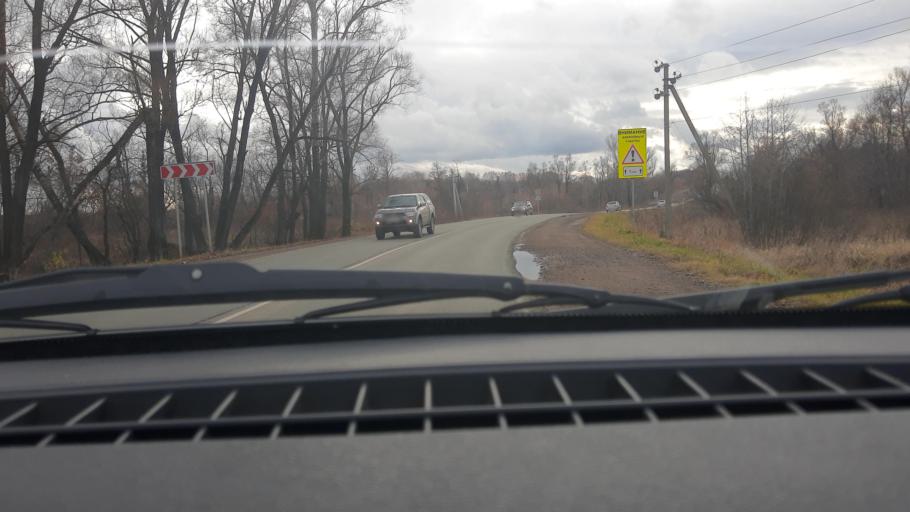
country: RU
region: Bashkortostan
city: Iglino
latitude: 54.8022
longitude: 56.3159
